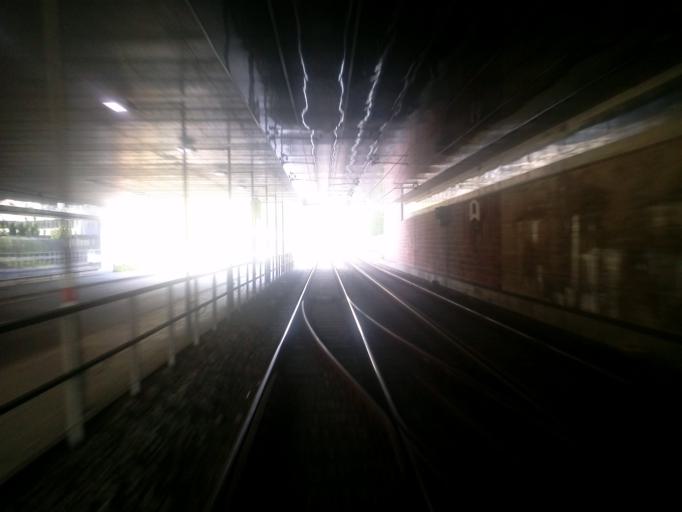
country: DE
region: Baden-Wuerttemberg
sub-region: Karlsruhe Region
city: Karlsruhe
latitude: 48.9923
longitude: 8.3968
